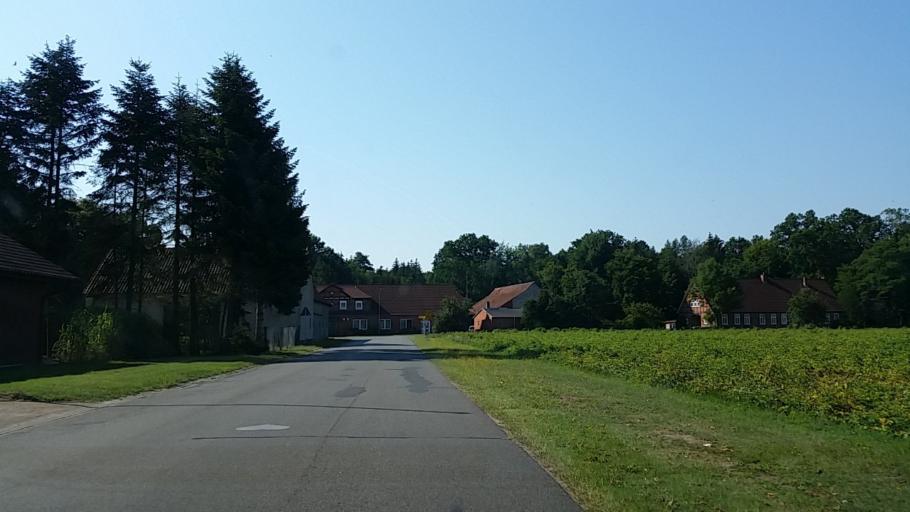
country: DE
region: Lower Saxony
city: Luder
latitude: 52.8099
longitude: 10.6295
